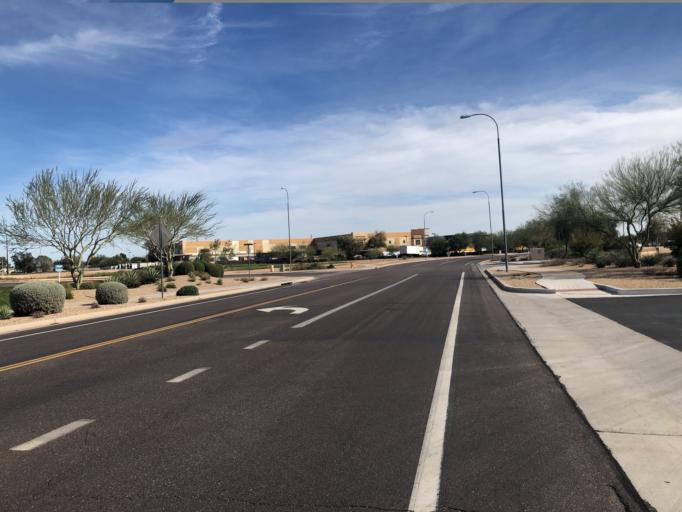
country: US
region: Arizona
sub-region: Maricopa County
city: San Carlos
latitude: 33.3108
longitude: -111.9149
